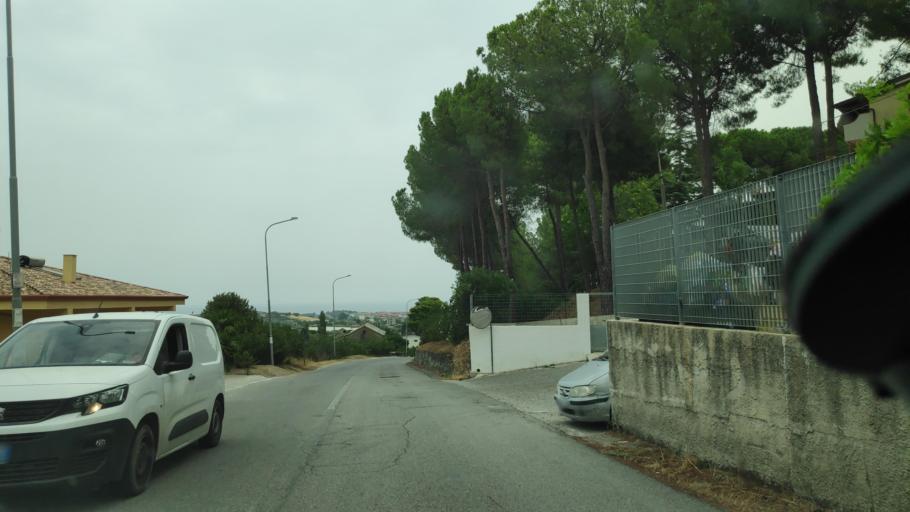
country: IT
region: Calabria
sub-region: Provincia di Catanzaro
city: Martelli-Laganosa
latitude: 38.6673
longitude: 16.5206
